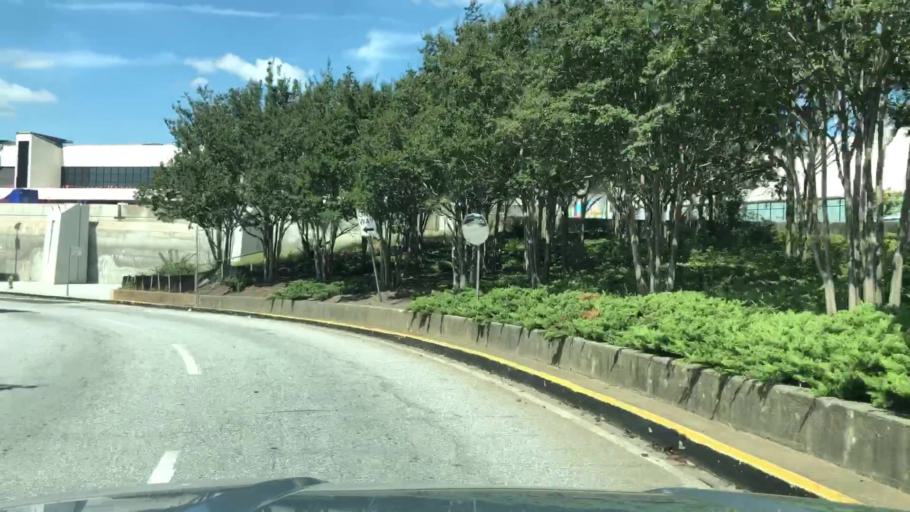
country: US
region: Georgia
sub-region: Fulton County
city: College Park
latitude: 33.6393
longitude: -84.4428
